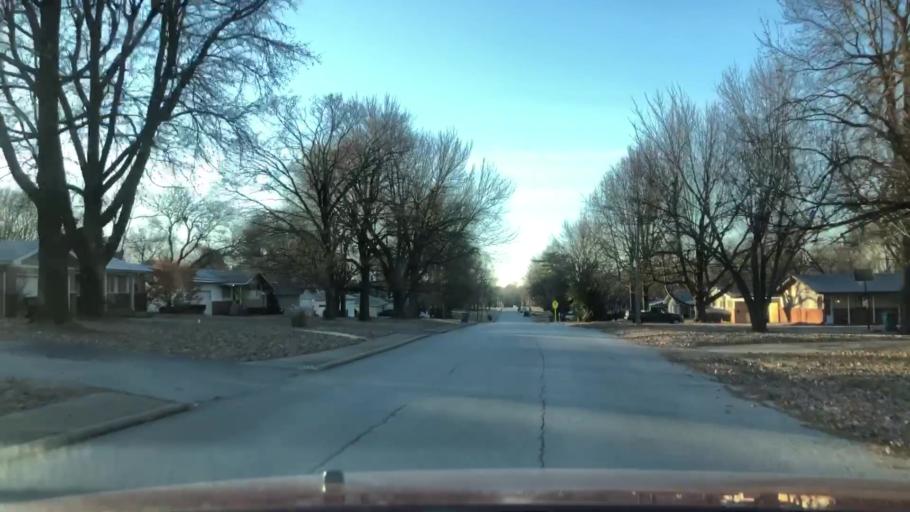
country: US
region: Missouri
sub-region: Greene County
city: Springfield
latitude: 37.1785
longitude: -93.2435
